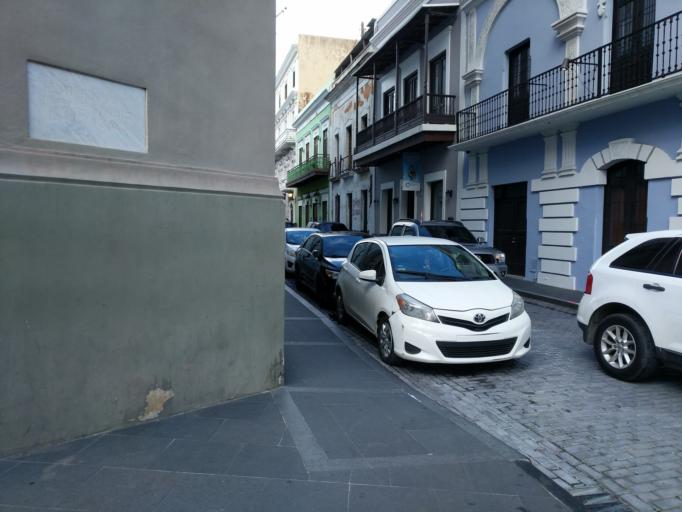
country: PR
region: San Juan
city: San Juan
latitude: 18.4640
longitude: -66.1169
